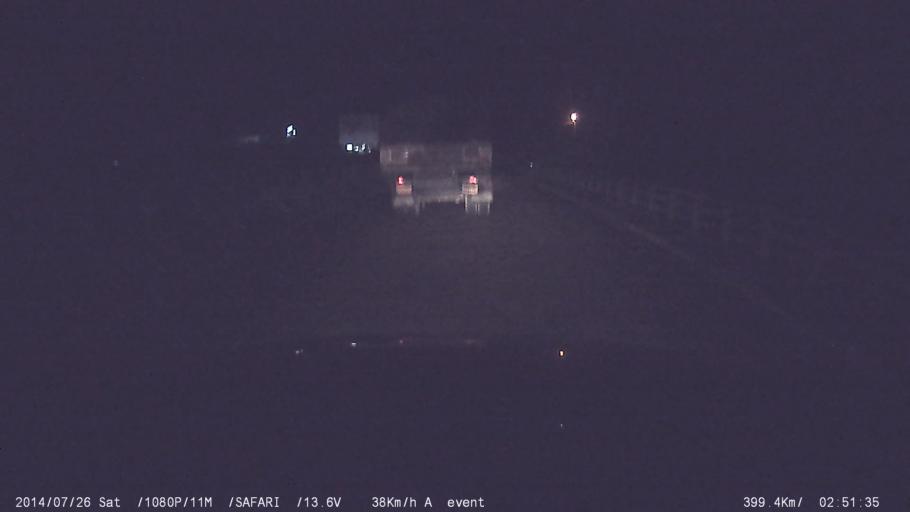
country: IN
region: Kerala
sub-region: Palakkad district
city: Palakkad
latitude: 10.7473
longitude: 76.6605
